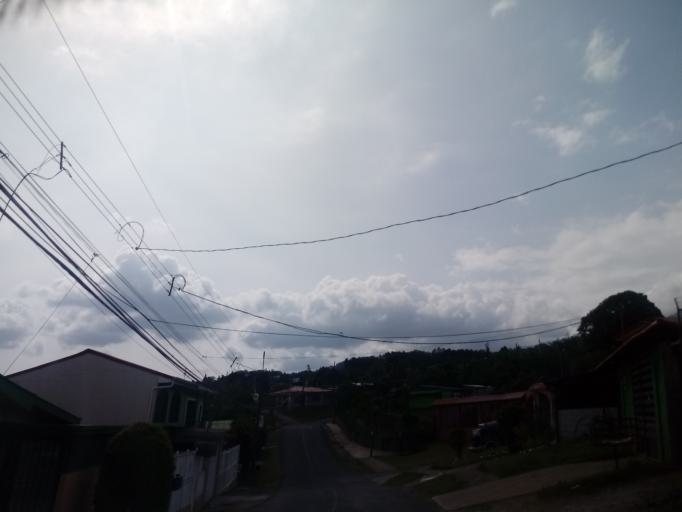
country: CR
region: Heredia
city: Angeles
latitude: 10.0231
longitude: -84.0469
